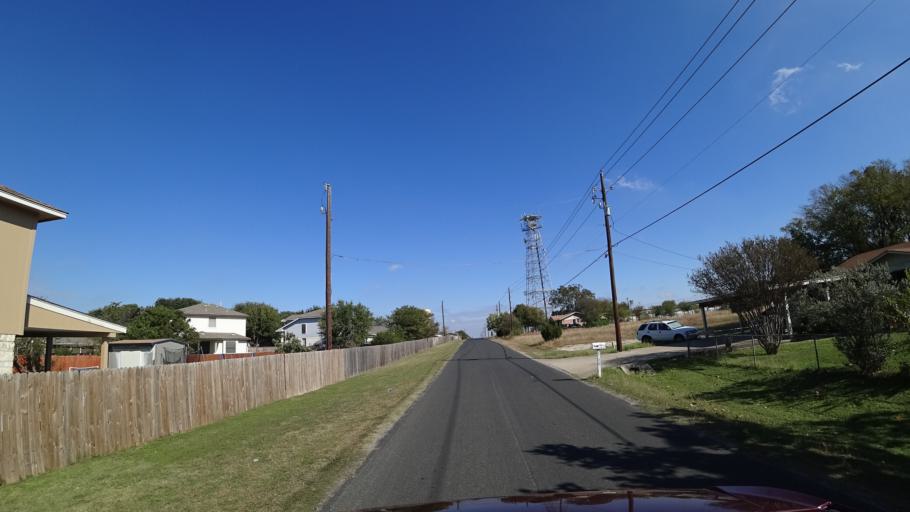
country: US
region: Texas
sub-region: Travis County
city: Windemere
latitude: 30.4430
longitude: -97.6544
